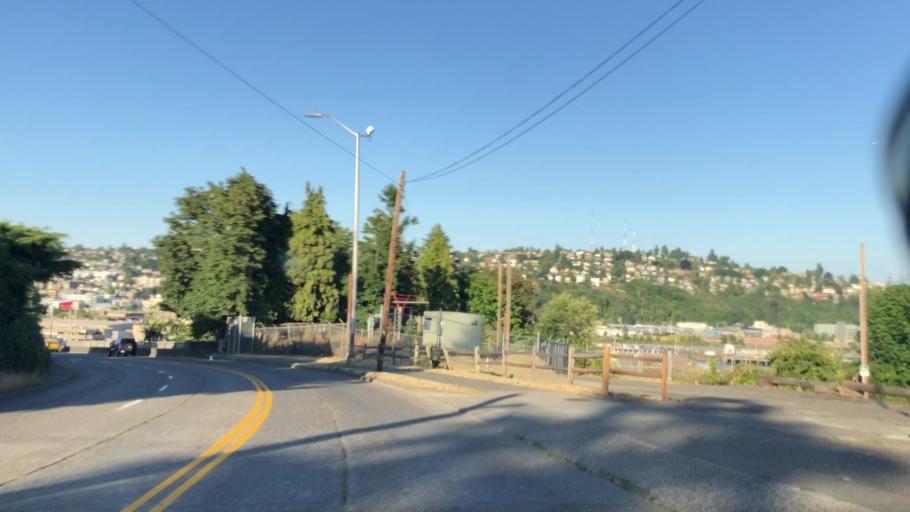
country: US
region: Washington
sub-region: King County
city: Seattle
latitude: 47.6323
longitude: -122.3905
